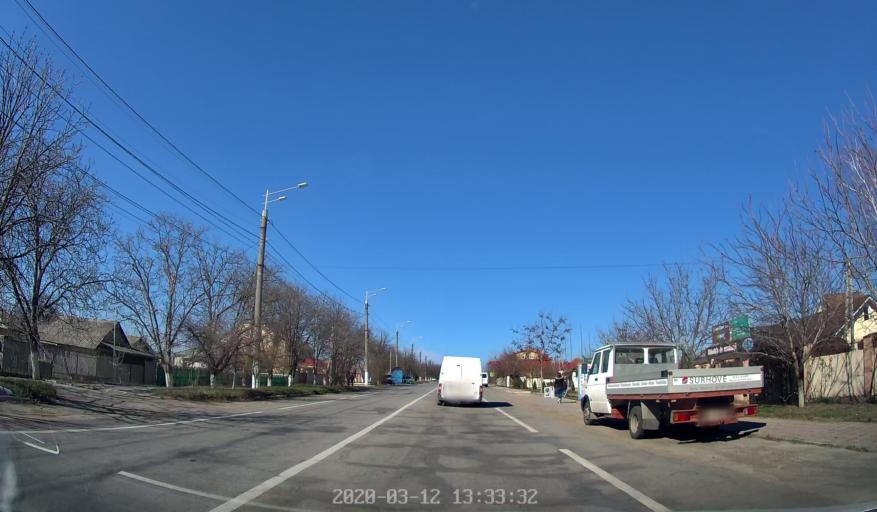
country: MD
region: Laloveni
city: Ialoveni
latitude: 46.9574
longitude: 28.7688
